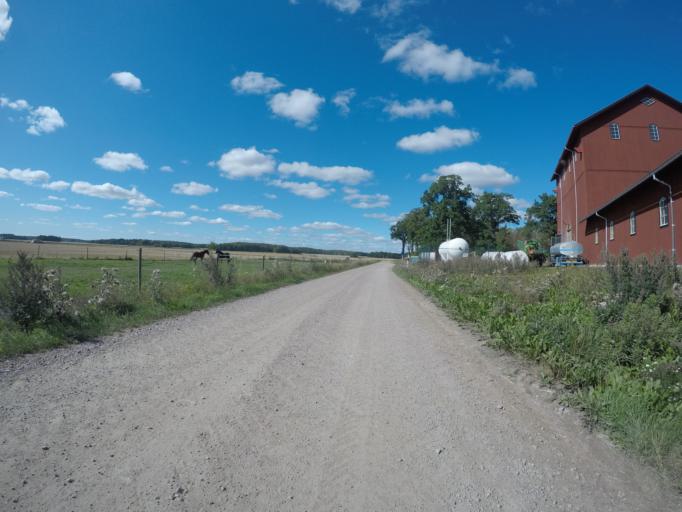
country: SE
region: Vaestmanland
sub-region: Hallstahammars Kommun
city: Kolback
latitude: 59.5118
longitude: 16.2468
